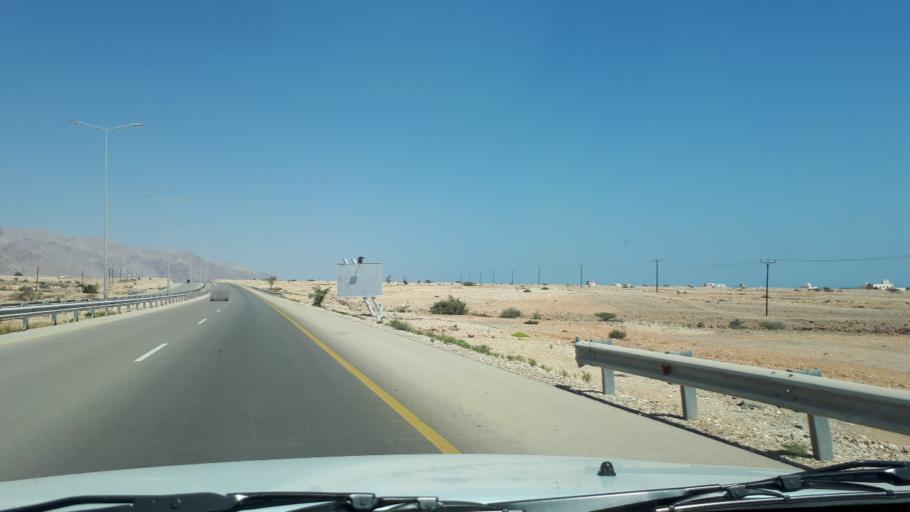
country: OM
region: Ash Sharqiyah
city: Sur
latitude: 22.7370
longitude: 59.3367
